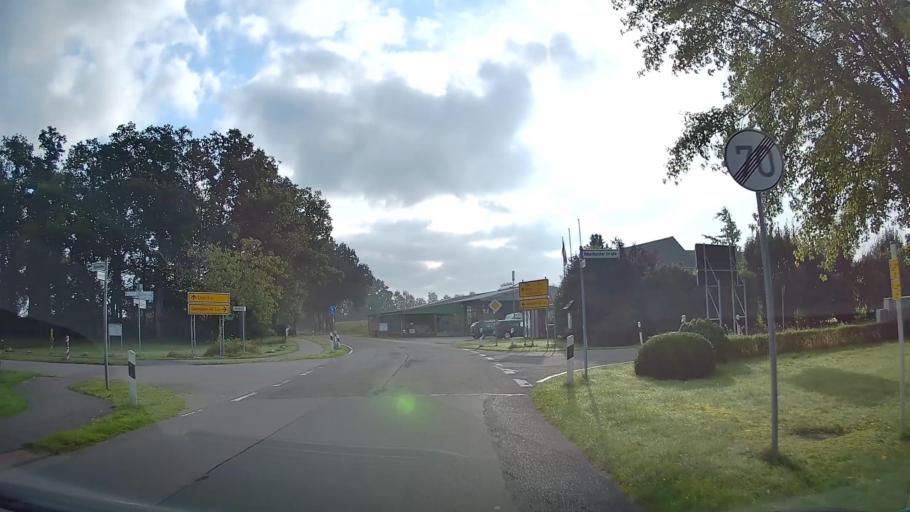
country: DE
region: Lower Saxony
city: Wardenburg
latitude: 53.0042
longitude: 8.1502
